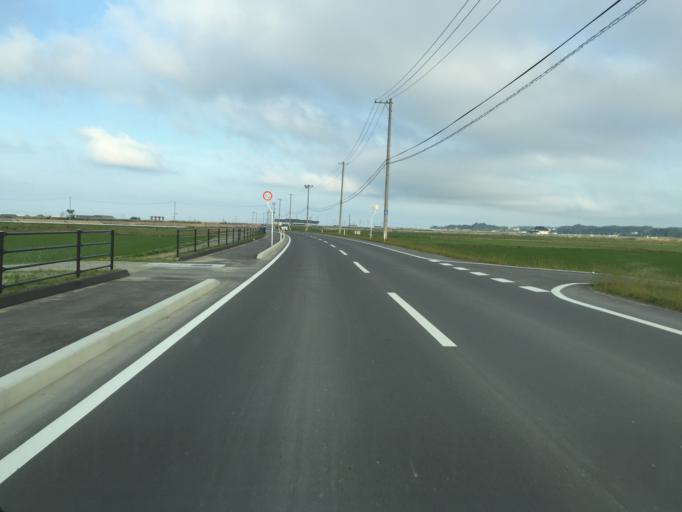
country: JP
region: Miyagi
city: Marumori
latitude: 37.7812
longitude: 140.9693
